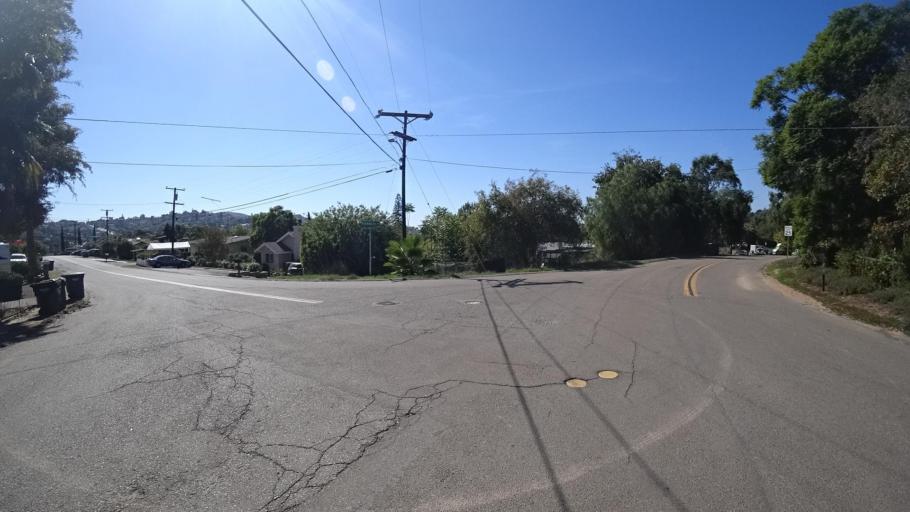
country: US
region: California
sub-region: San Diego County
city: Casa de Oro-Mount Helix
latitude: 32.7508
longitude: -116.9789
